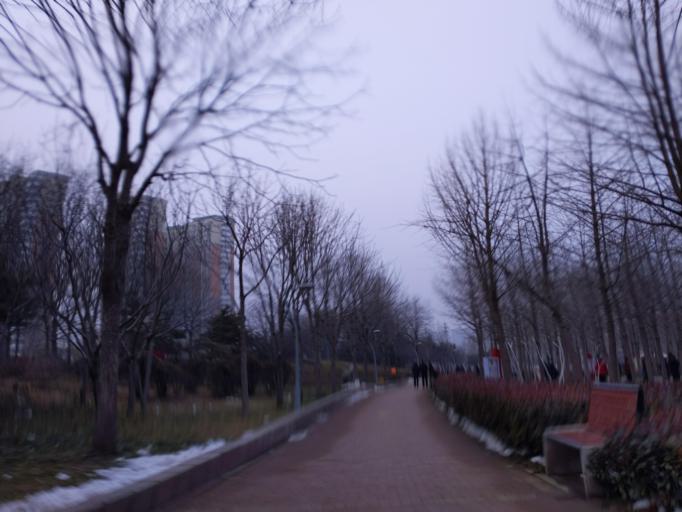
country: CN
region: Henan Sheng
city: Puyang
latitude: 35.7786
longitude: 115.0282
